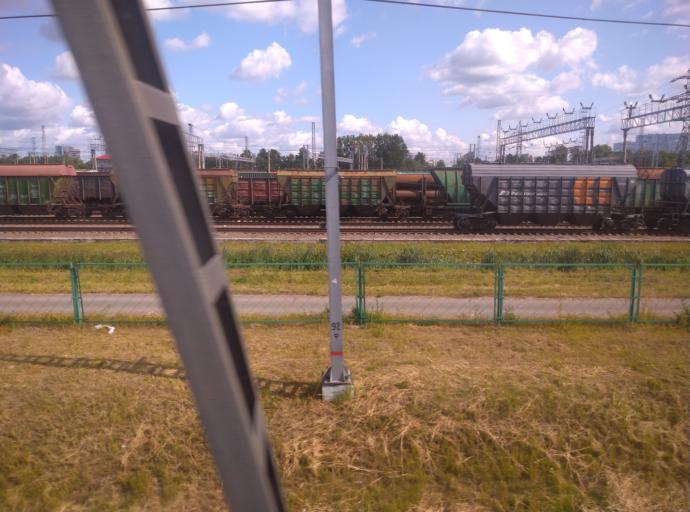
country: RU
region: St.-Petersburg
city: Obukhovo
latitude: 59.8609
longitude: 30.4347
